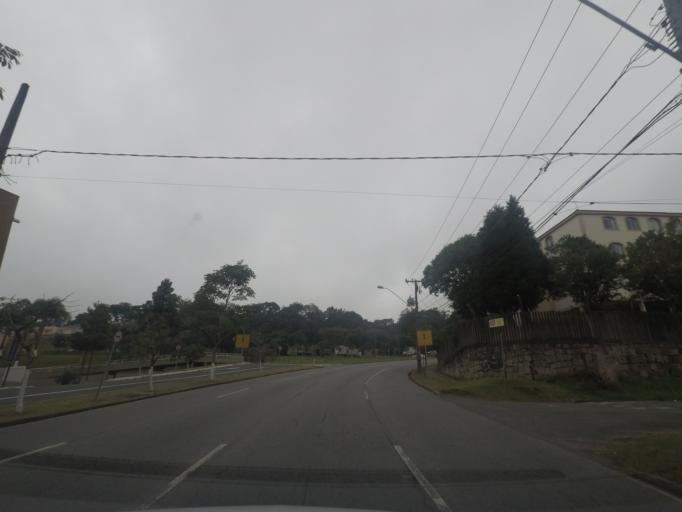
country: BR
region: Parana
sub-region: Curitiba
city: Curitiba
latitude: -25.3778
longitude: -49.2221
